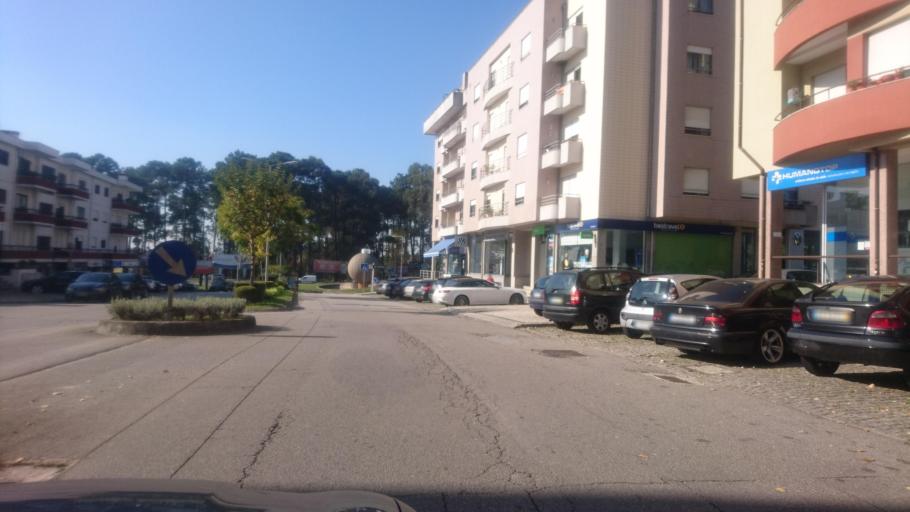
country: PT
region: Aveiro
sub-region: Santa Maria da Feira
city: Feira
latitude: 40.9246
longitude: -8.5637
